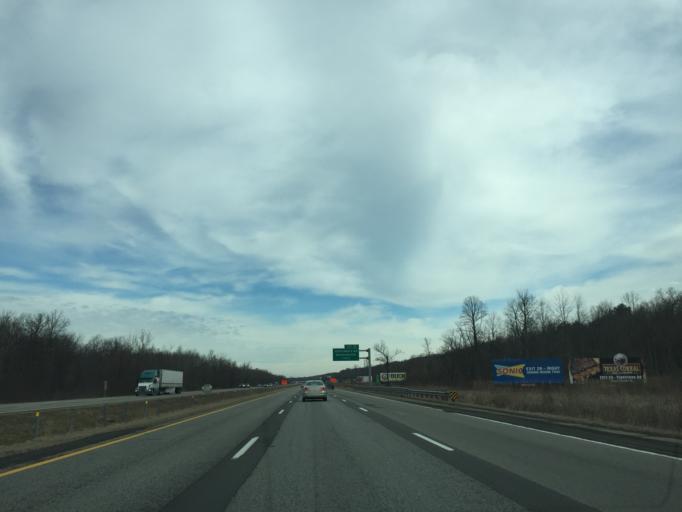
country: US
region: Michigan
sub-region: Berrien County
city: Stevensville
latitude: 41.9911
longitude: -86.5393
